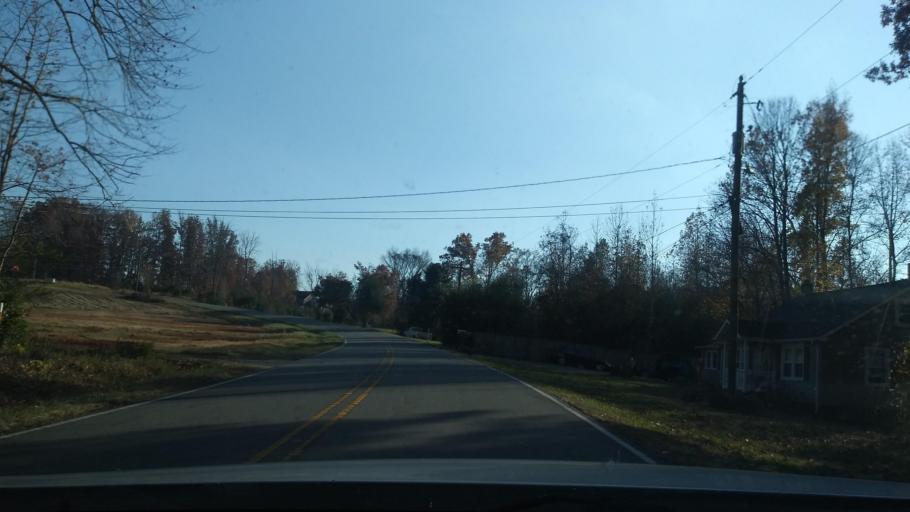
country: US
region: North Carolina
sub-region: Rockingham County
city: Reidsville
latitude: 36.3049
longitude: -79.7397
